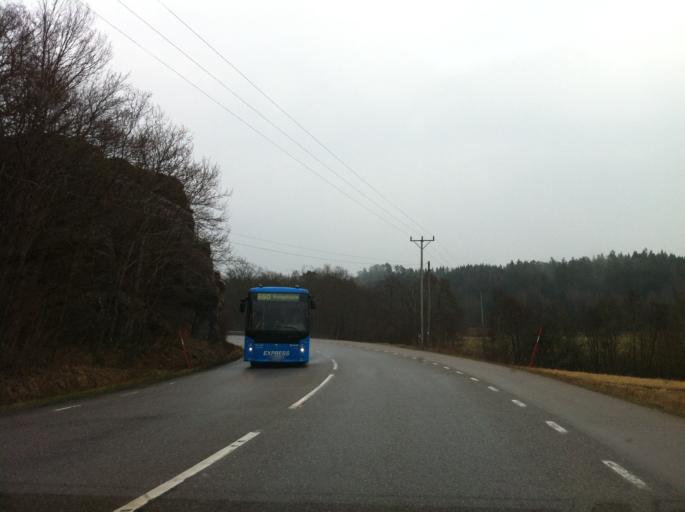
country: SE
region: Vaestra Goetaland
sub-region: Lysekils Kommun
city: Brastad
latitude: 58.4553
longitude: 11.4675
